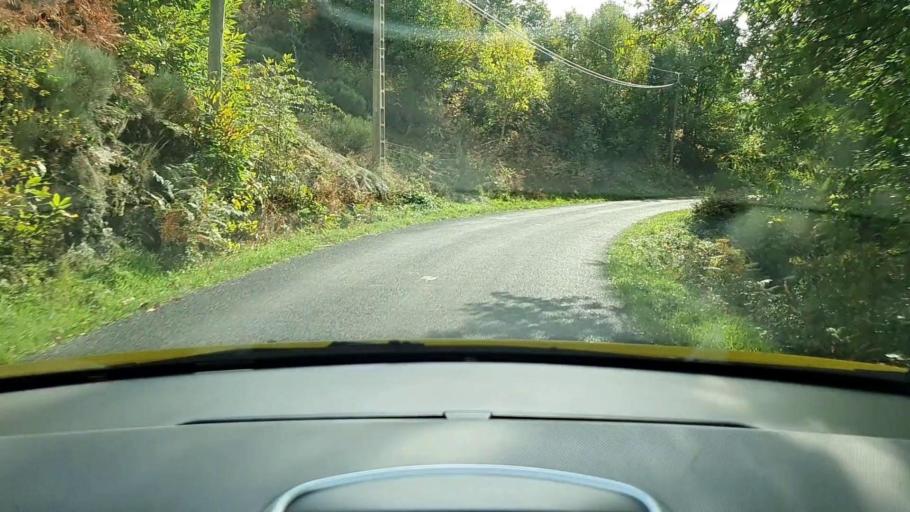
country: FR
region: Languedoc-Roussillon
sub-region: Departement de la Lozere
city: Meyrueis
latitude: 44.0700
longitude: 3.4568
